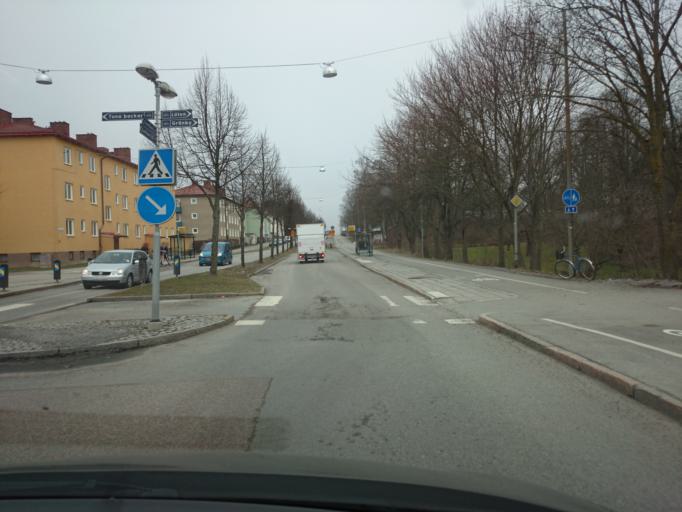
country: SE
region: Uppsala
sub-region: Uppsala Kommun
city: Uppsala
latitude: 59.8750
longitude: 17.6249
